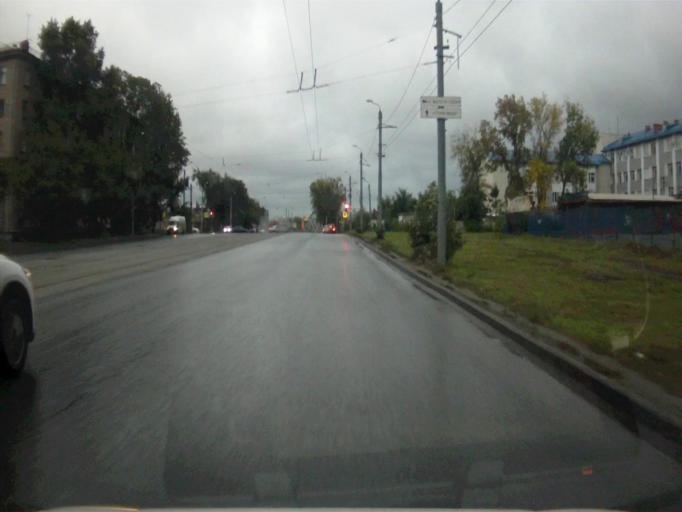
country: RU
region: Chelyabinsk
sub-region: Gorod Chelyabinsk
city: Chelyabinsk
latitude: 55.1587
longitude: 61.4448
